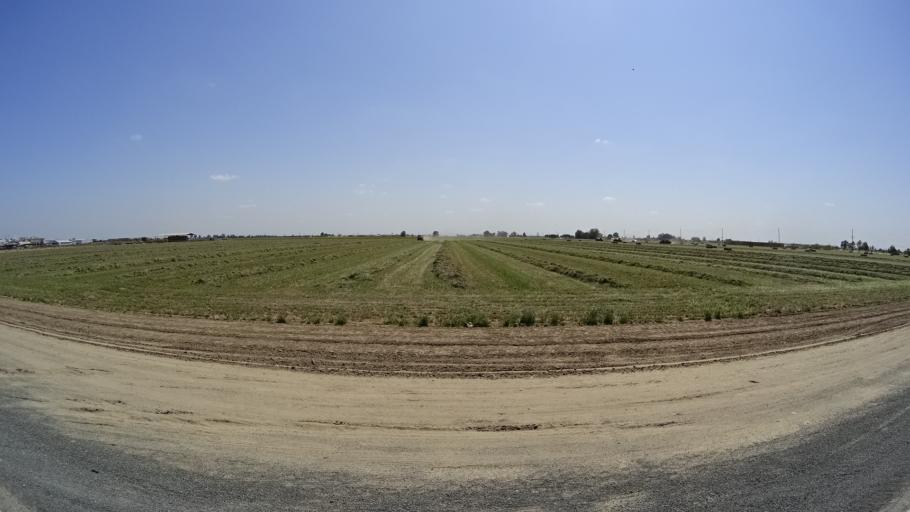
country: US
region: California
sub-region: Kings County
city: Home Garden
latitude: 36.3159
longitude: -119.6190
